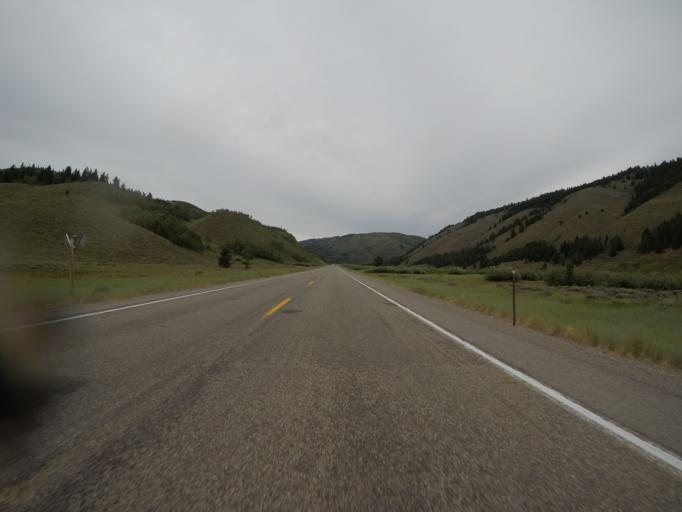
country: US
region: Wyoming
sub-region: Lincoln County
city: Afton
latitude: 42.4729
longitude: -110.9660
